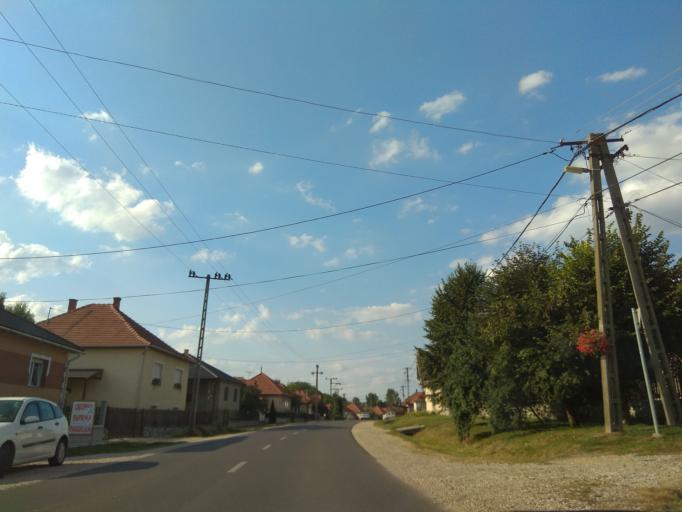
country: HU
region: Borsod-Abauj-Zemplen
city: Harsany
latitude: 47.9683
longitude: 20.7409
